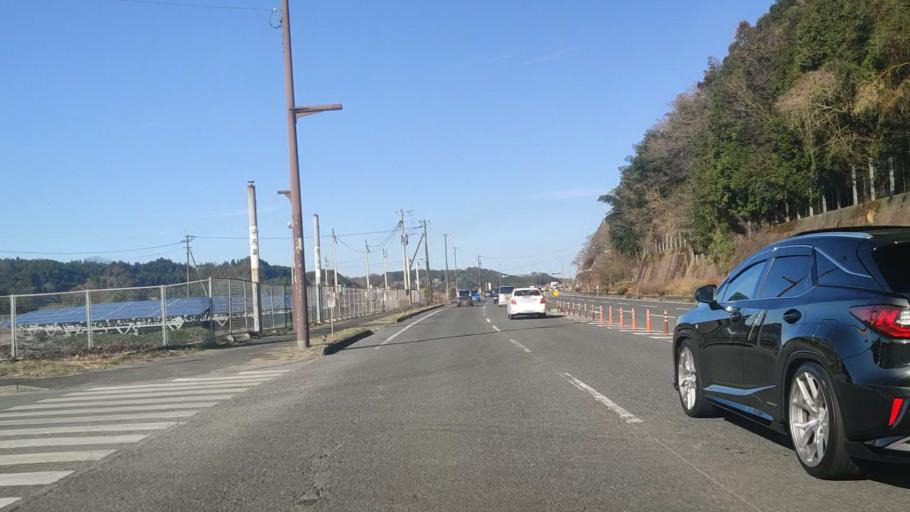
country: JP
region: Oita
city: Oita
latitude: 33.1174
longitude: 131.6536
